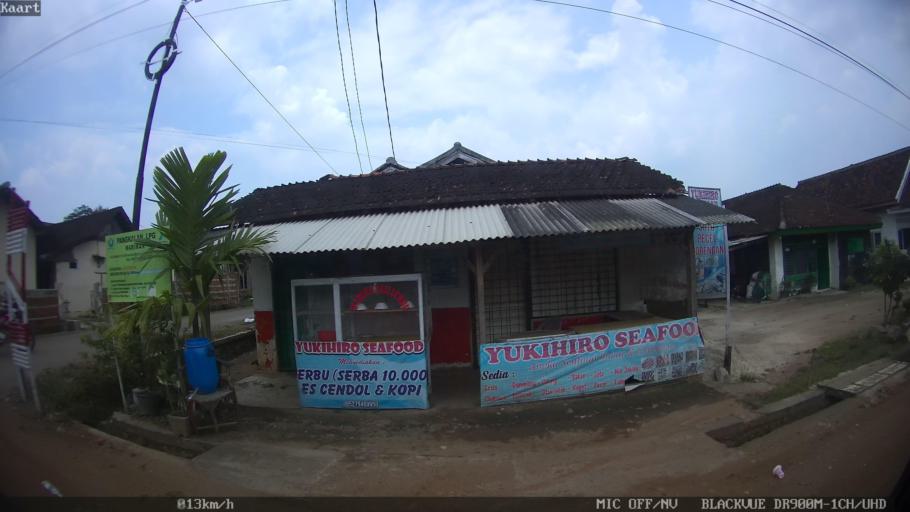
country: ID
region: Lampung
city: Gadingrejo
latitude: -5.3644
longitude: 105.0256
